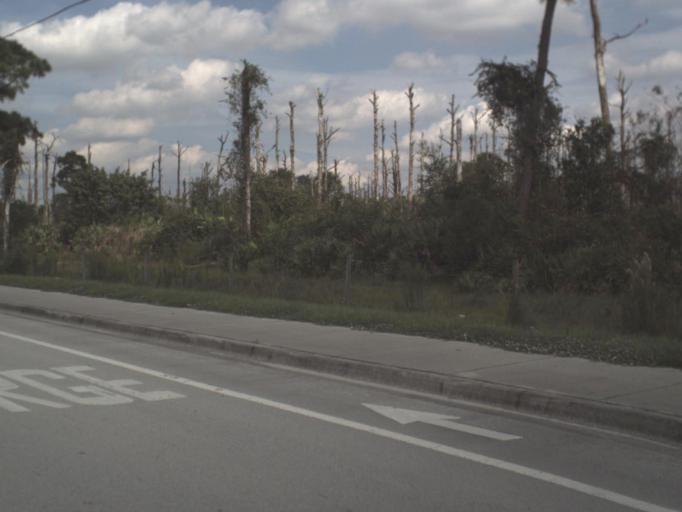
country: US
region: Florida
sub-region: Okeechobee County
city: Cypress Quarters
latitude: 27.2756
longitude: -80.8289
